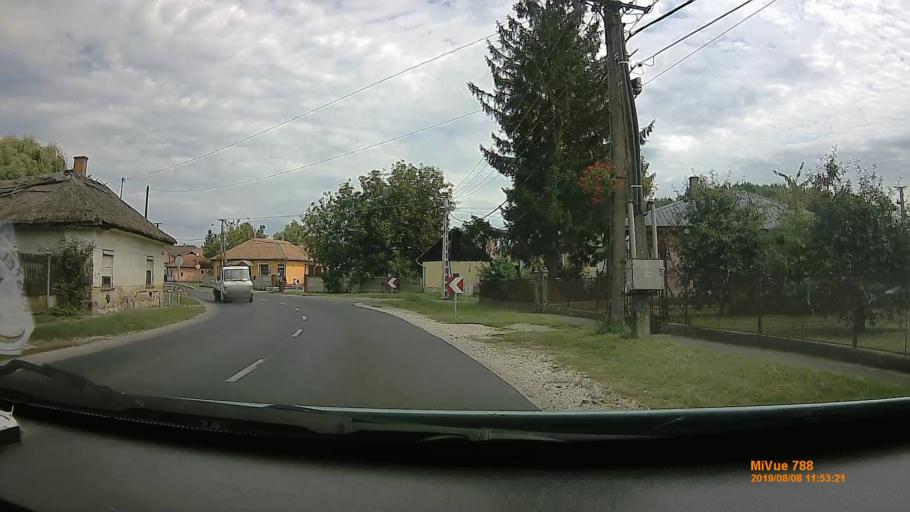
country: HU
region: Szabolcs-Szatmar-Bereg
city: Nyirmihalydi
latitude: 47.7319
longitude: 21.9606
